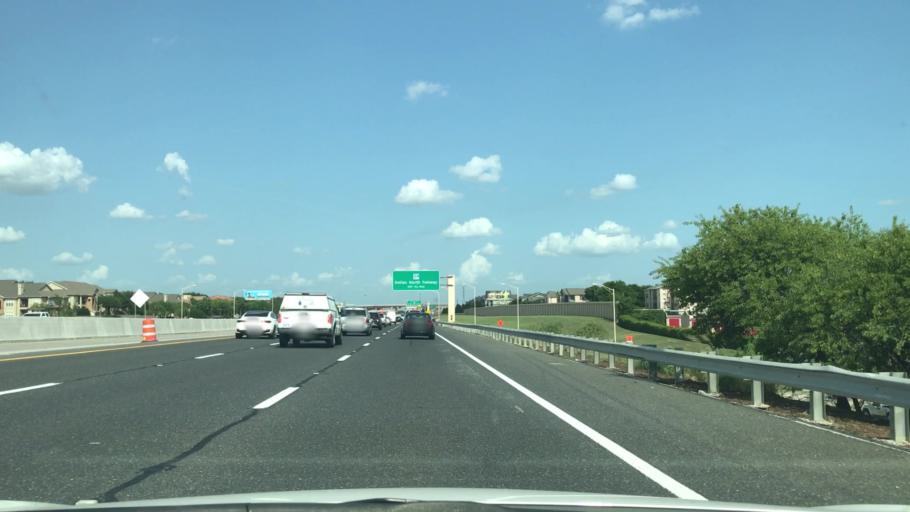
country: US
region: Texas
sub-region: Dallas County
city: Addison
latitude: 33.0119
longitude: -96.8421
